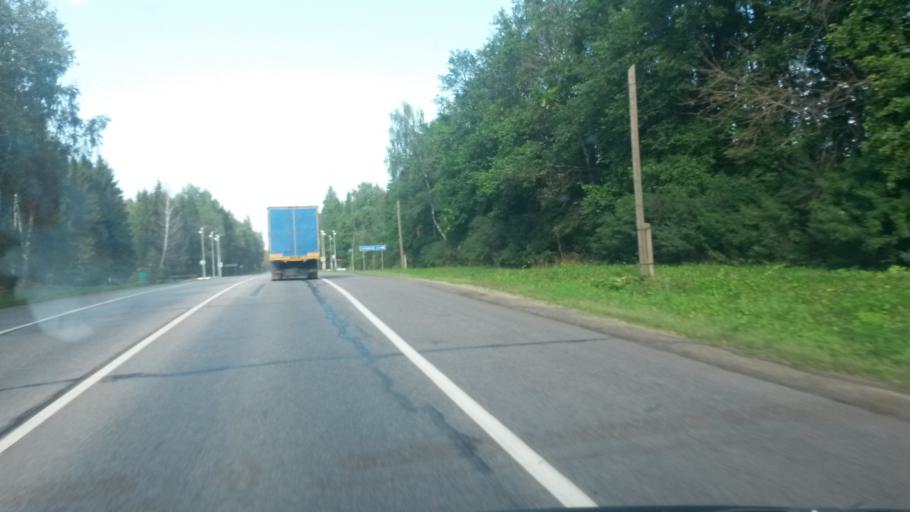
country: RU
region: Jaroslavl
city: Pereslavl'-Zalesskiy
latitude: 56.6434
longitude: 38.6868
